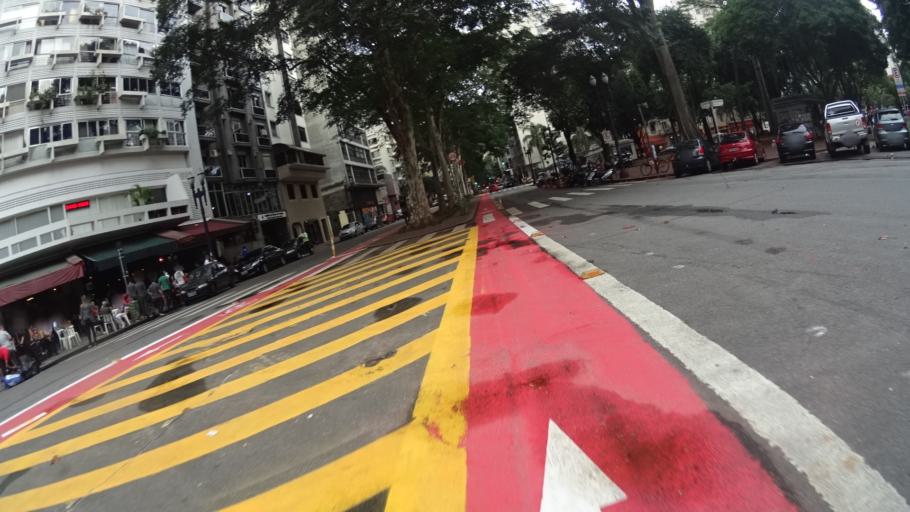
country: BR
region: Sao Paulo
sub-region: Sao Paulo
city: Sao Paulo
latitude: -23.5405
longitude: -46.6451
